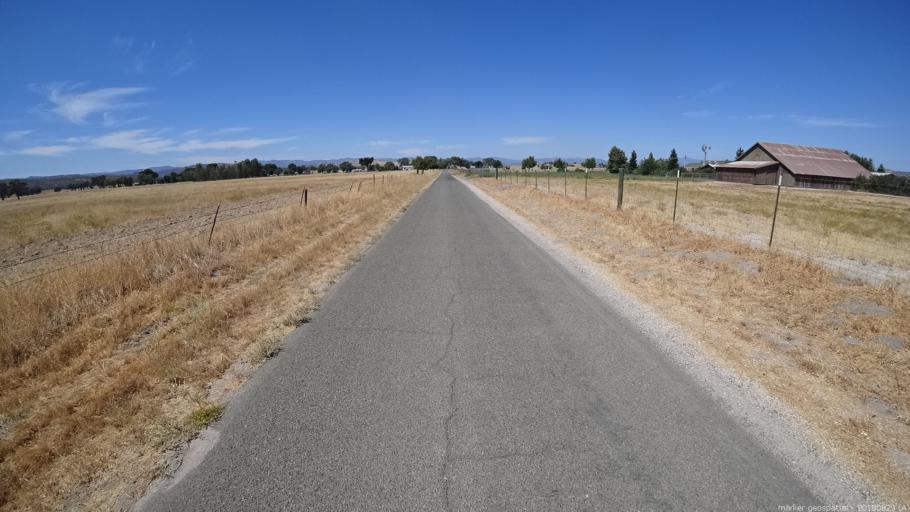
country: US
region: California
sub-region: Monterey County
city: King City
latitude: 35.9440
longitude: -121.0781
